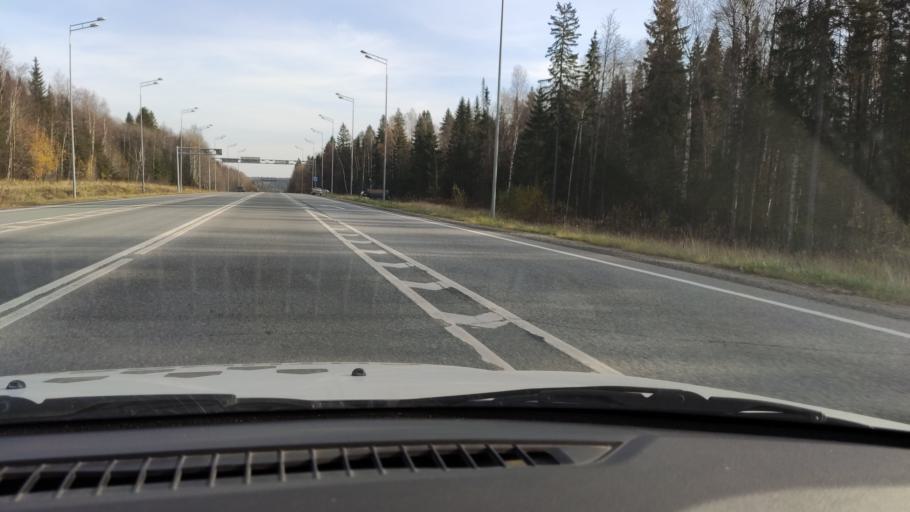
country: RU
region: Perm
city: Novyye Lyady
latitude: 58.0433
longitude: 56.4429
